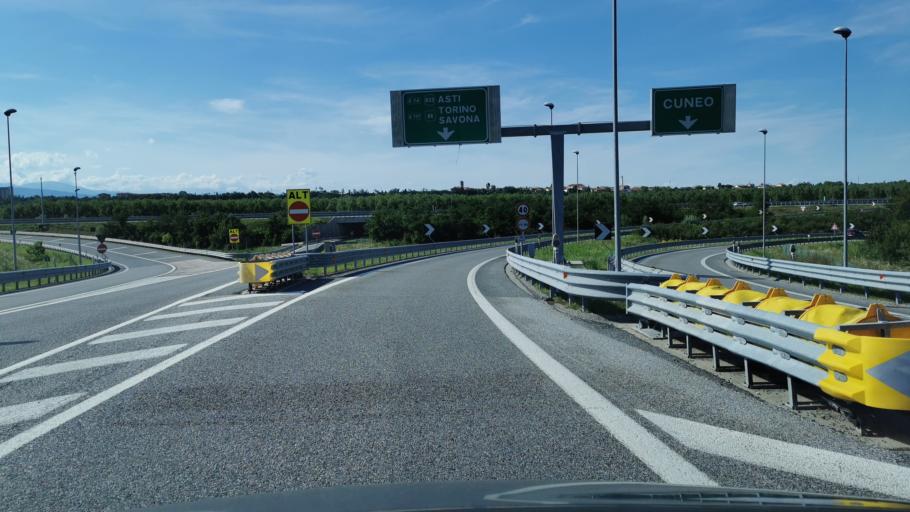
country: IT
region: Piedmont
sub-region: Provincia di Cuneo
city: Cuneo
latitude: 44.4221
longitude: 7.5908
